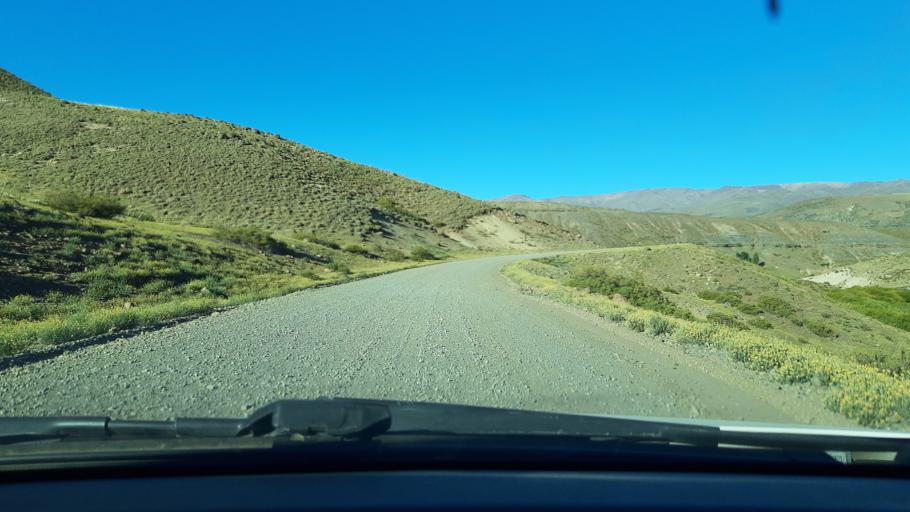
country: AR
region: Neuquen
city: Las Ovejas
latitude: -36.8218
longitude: -70.7046
